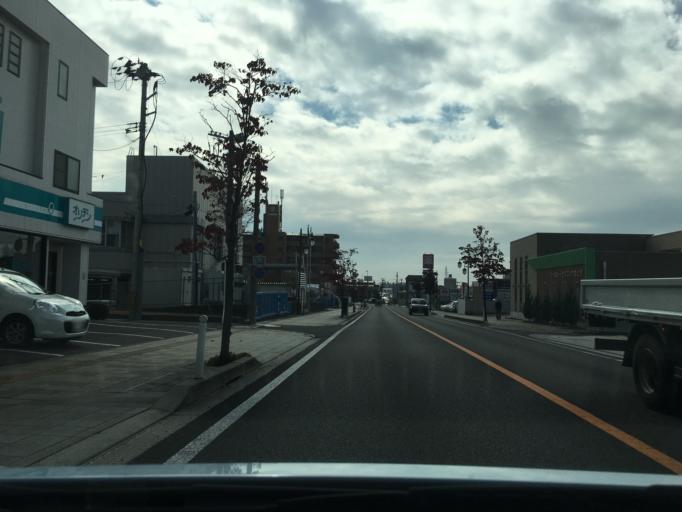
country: JP
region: Fukushima
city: Koriyama
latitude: 37.3890
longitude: 140.3553
